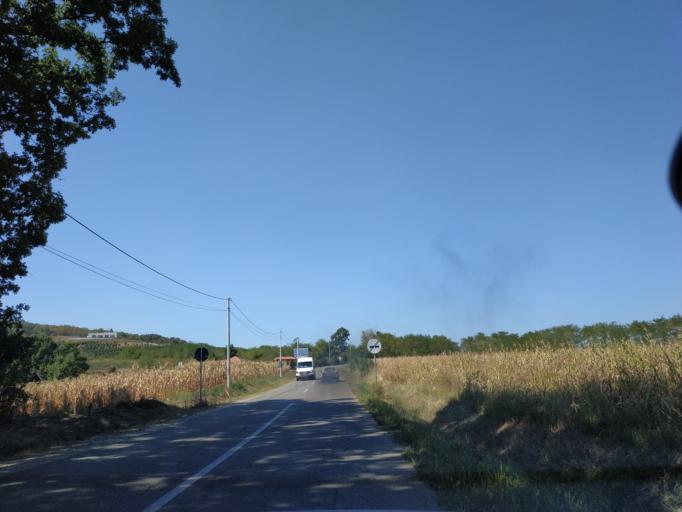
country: RS
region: Central Serbia
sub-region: Sumadijski Okrug
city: Topola
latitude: 44.2687
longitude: 20.6555
